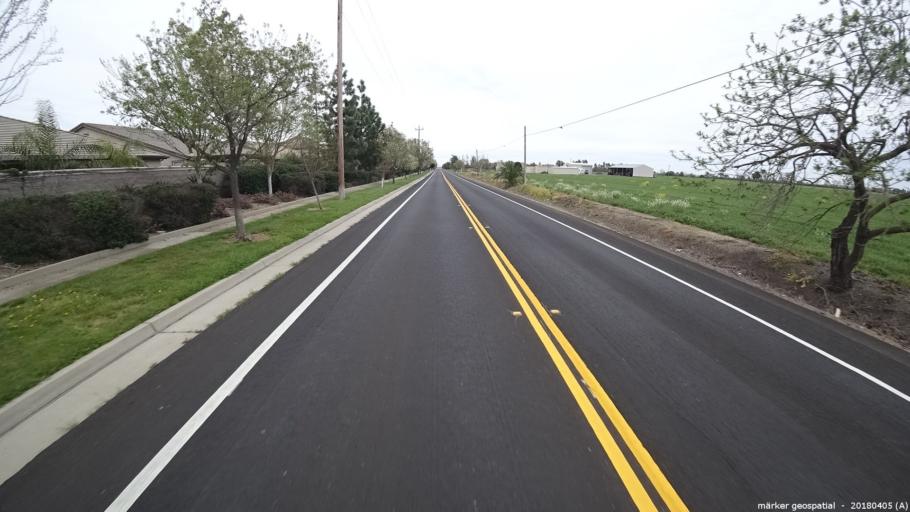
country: US
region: California
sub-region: Sacramento County
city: Laguna
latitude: 38.3794
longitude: -121.4263
